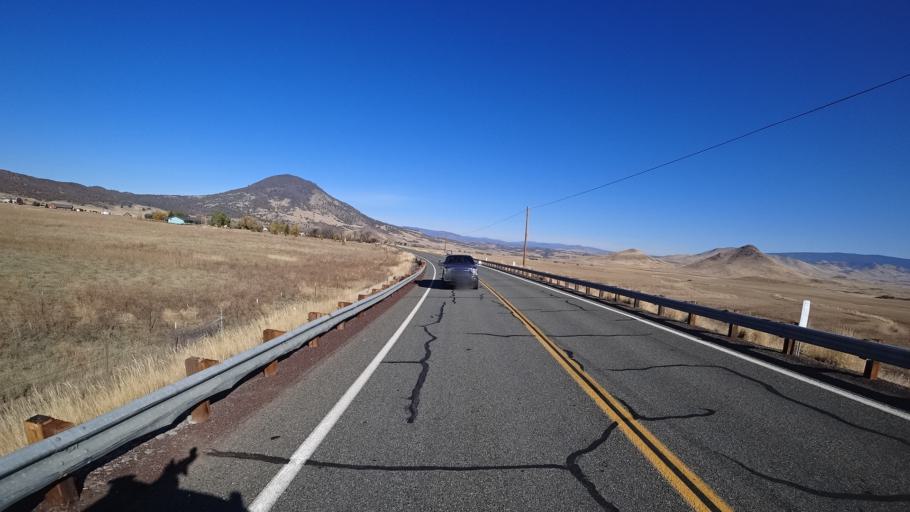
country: US
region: California
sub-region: Siskiyou County
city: Montague
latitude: 41.8079
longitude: -122.4987
